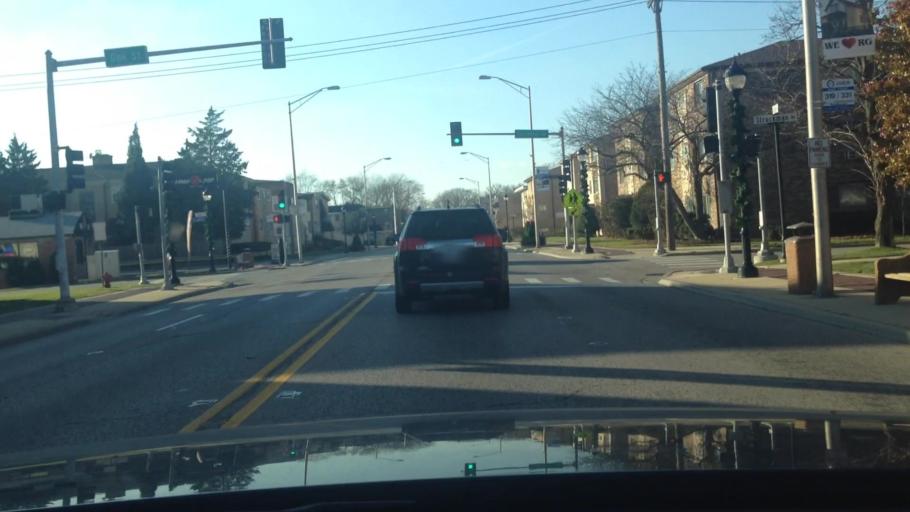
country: US
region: Illinois
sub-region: Cook County
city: River Grove
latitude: 41.9294
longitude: -87.8401
